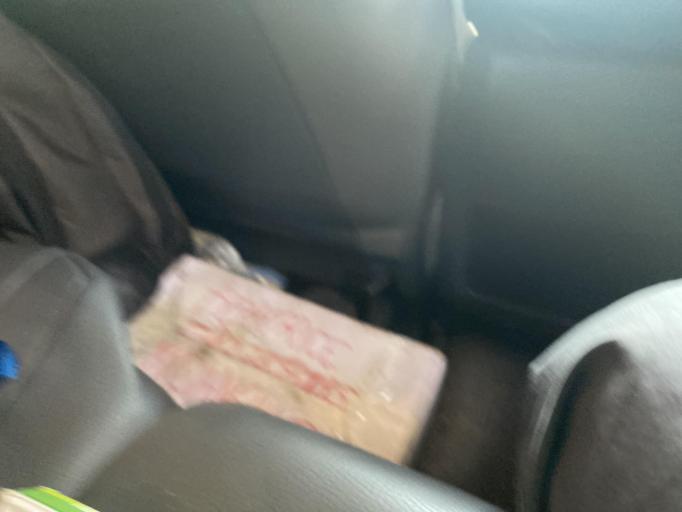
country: CD
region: Kasai-Oriental
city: Mbuji-Mayi
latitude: -6.2456
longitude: 23.7578
